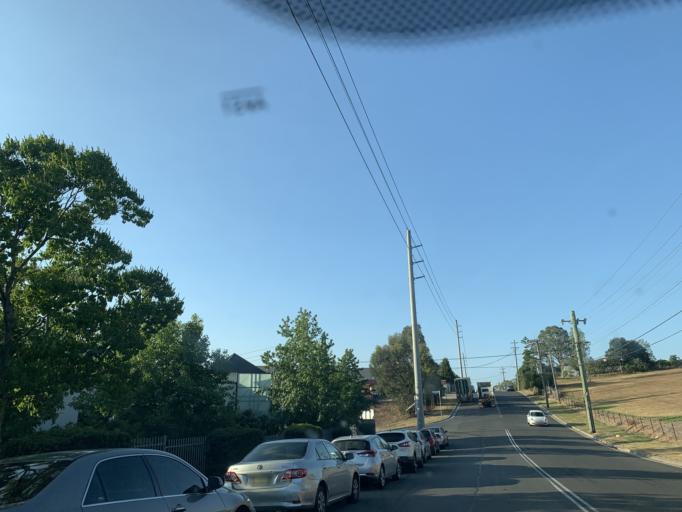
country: AU
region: New South Wales
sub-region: Fairfield
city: Horsley Park
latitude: -33.8383
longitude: 150.8810
